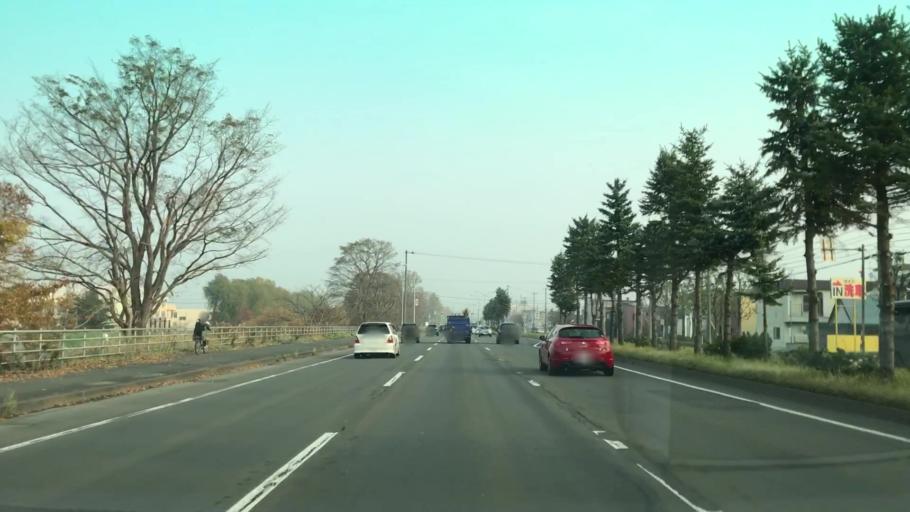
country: JP
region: Hokkaido
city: Sapporo
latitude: 43.1512
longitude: 141.3511
